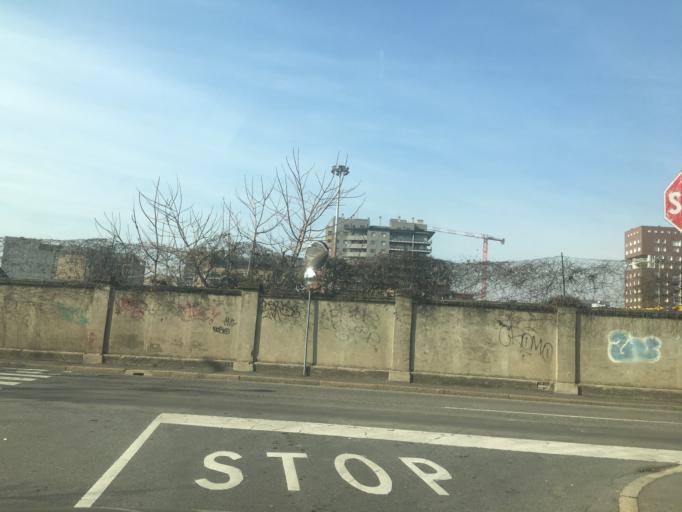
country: IT
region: Lombardy
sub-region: Citta metropolitana di Milano
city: Sesto San Giovanni
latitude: 45.5145
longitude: 9.2180
